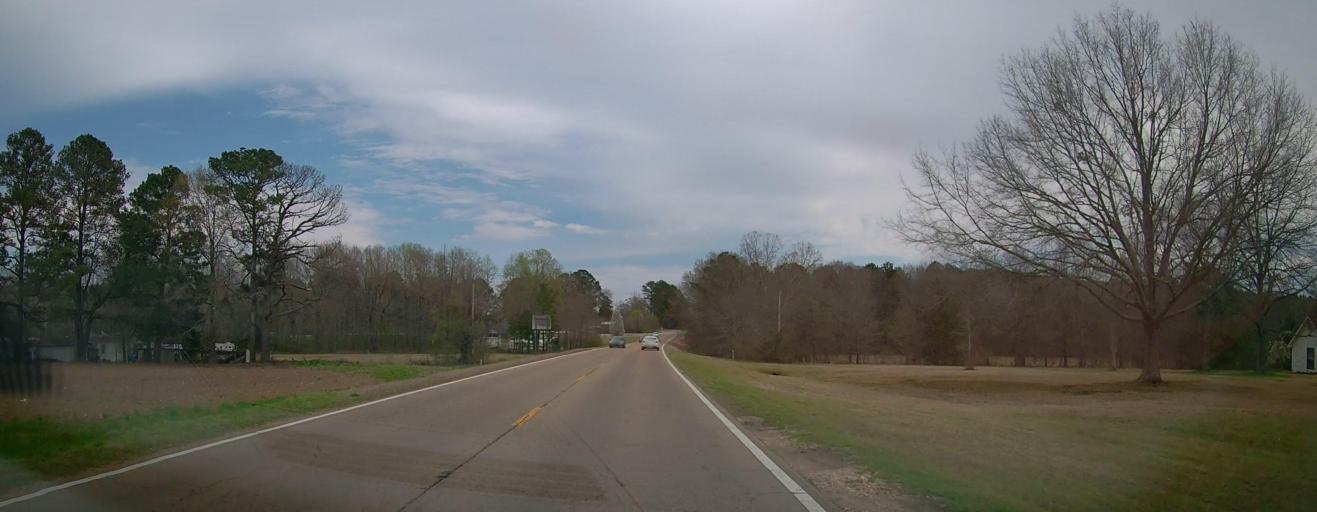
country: US
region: Mississippi
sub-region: Itawamba County
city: Mantachie
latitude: 34.2668
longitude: -88.5565
